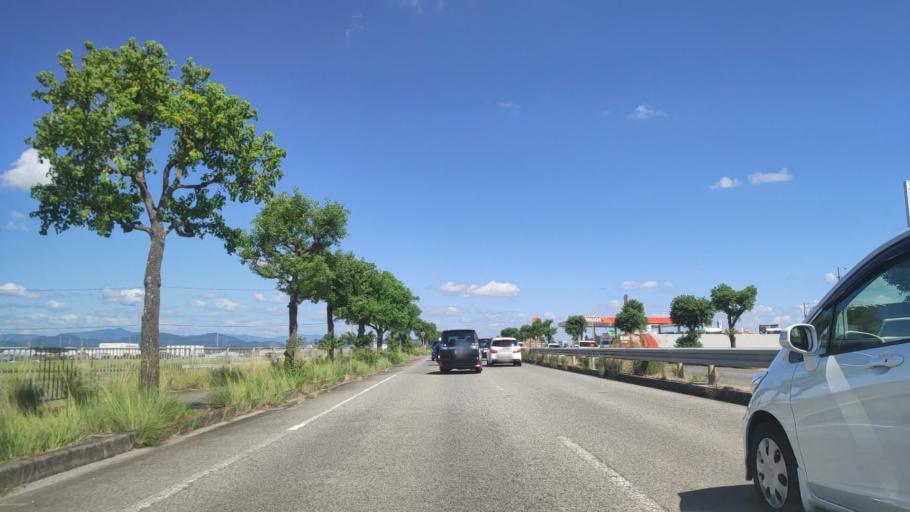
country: JP
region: Hyogo
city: Ono
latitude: 34.8633
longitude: 134.9522
